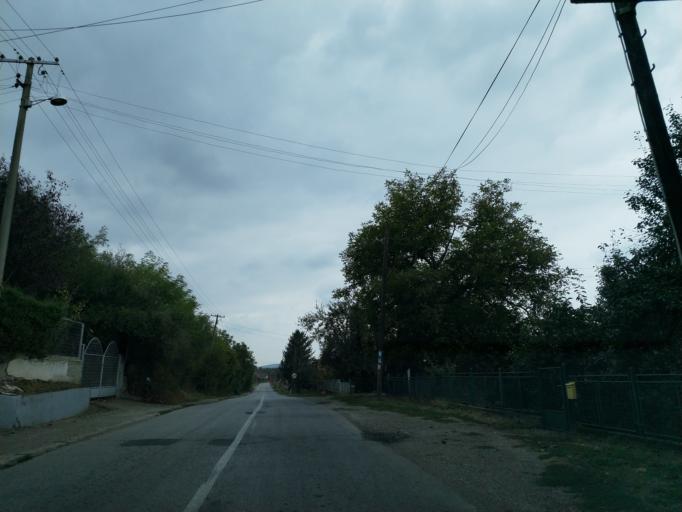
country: RS
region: Central Serbia
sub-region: Pomoravski Okrug
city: Jagodina
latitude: 44.0729
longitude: 21.1793
